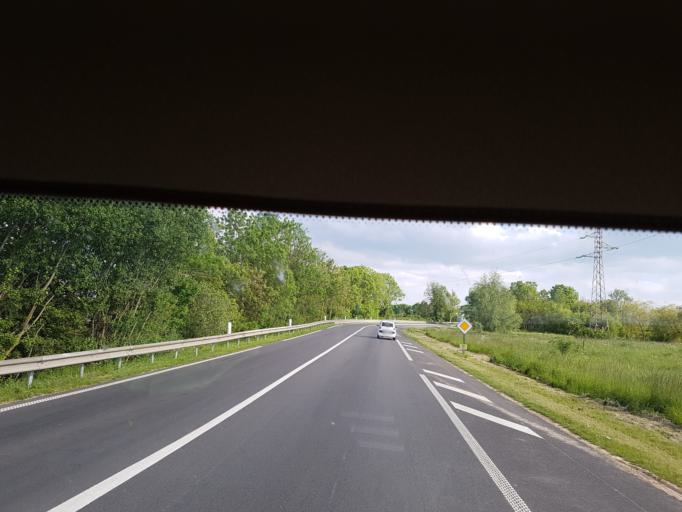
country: FR
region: Nord-Pas-de-Calais
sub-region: Departement du Pas-de-Calais
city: Hesdin
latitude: 50.3639
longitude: 2.0384
